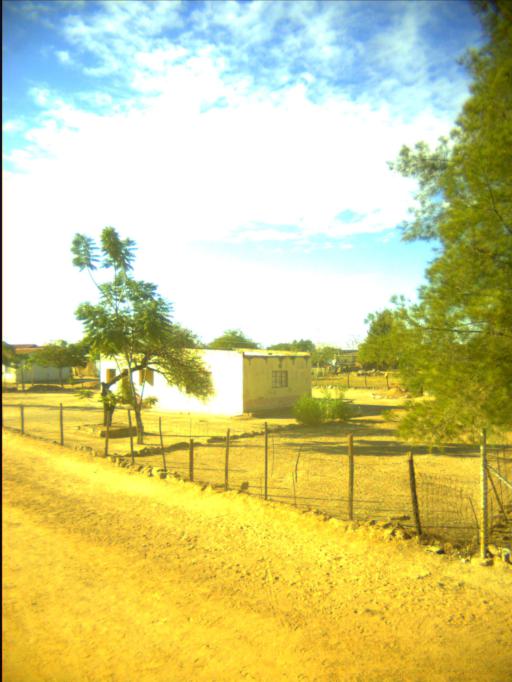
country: ZA
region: Mpumalanga
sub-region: Nkangala District Municipality
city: Siyabuswa
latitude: -25.1507
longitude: 28.9695
